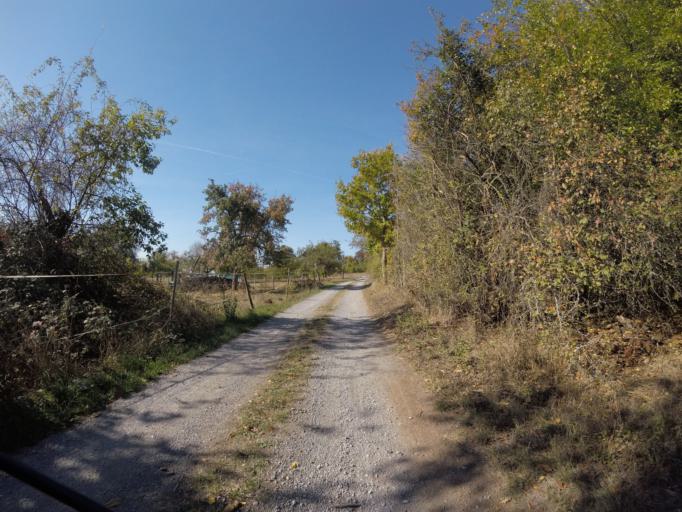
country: DE
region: Baden-Wuerttemberg
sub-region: Karlsruhe Region
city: Sternenfels
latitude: 49.0145
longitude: 8.8508
